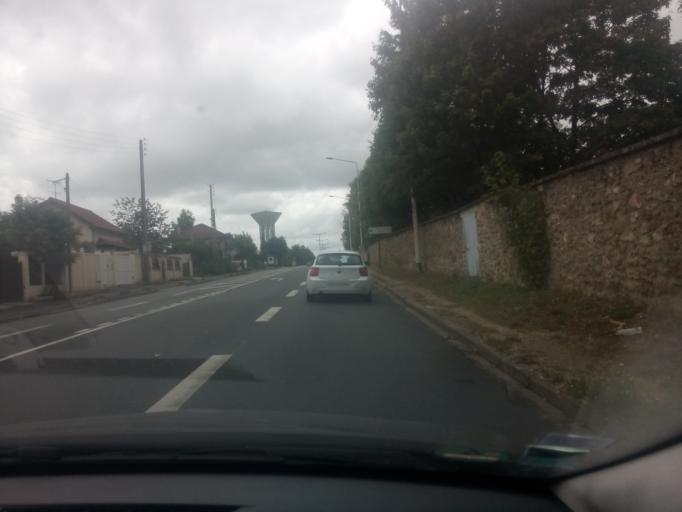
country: FR
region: Ile-de-France
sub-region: Departement des Yvelines
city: Jouy-en-Josas
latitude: 48.7576
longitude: 2.1732
